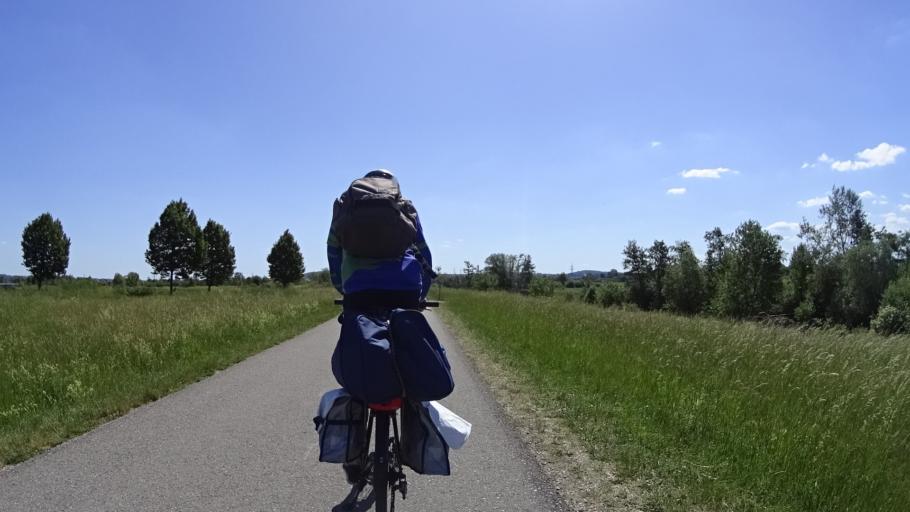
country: DE
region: Bavaria
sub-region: Regierungsbezirk Mittelfranken
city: Gunzenhausen
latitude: 49.1198
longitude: 10.7300
